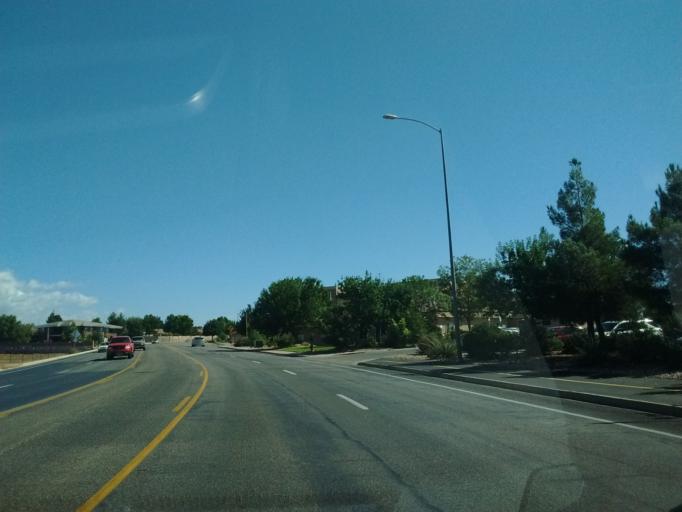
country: US
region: Utah
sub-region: Washington County
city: Saint George
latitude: 37.0872
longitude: -113.5619
